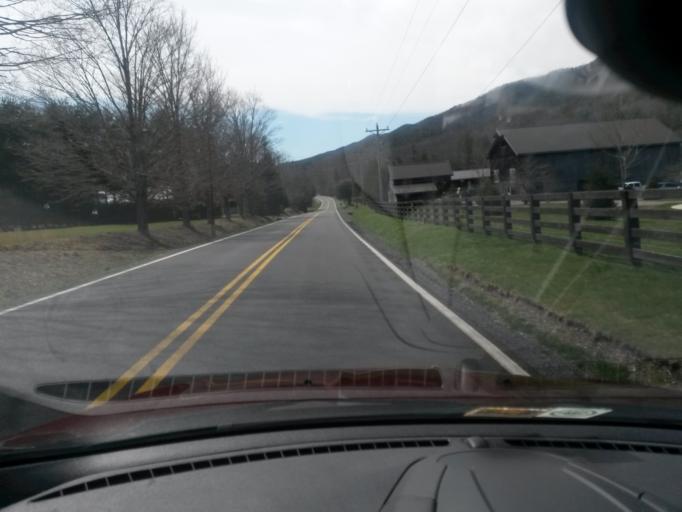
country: US
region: West Virginia
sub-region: Greenbrier County
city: White Sulphur Springs
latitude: 37.6922
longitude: -80.2197
